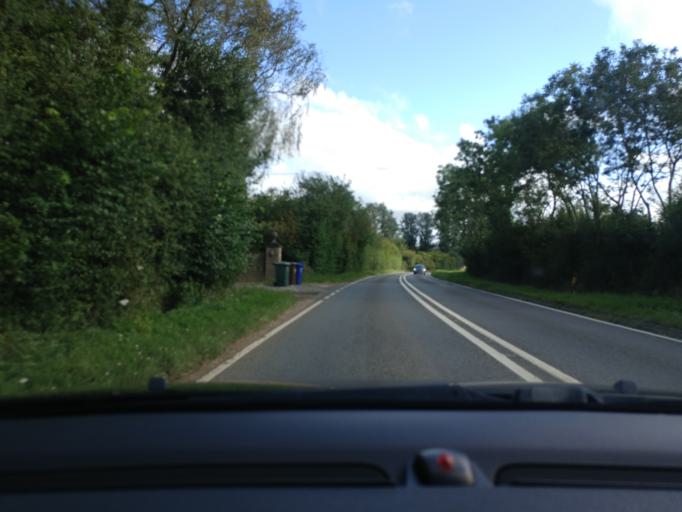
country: GB
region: England
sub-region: Oxfordshire
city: Kidlington
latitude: 51.8690
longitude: -1.2272
